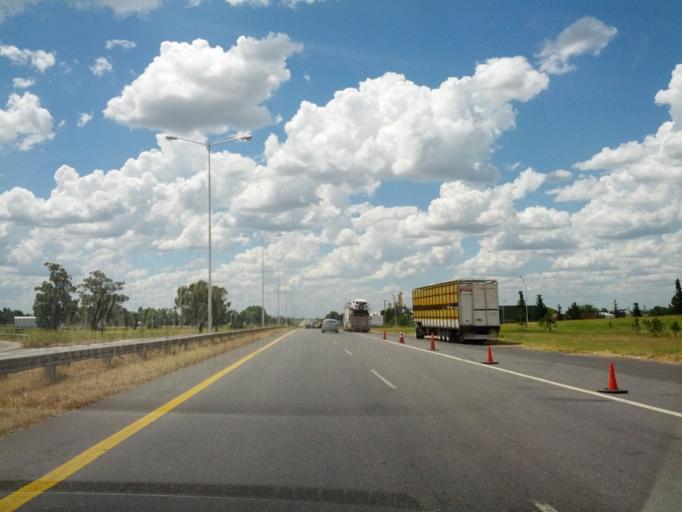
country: AR
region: Entre Rios
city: Gualeguaychu
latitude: -33.0394
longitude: -58.6182
